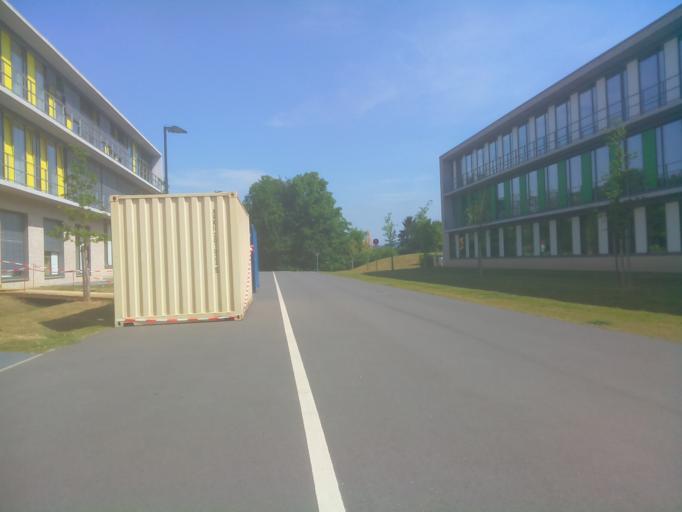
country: DE
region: Baden-Wuerttemberg
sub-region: Karlsruhe Region
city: Weinheim
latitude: 49.5496
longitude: 8.6463
